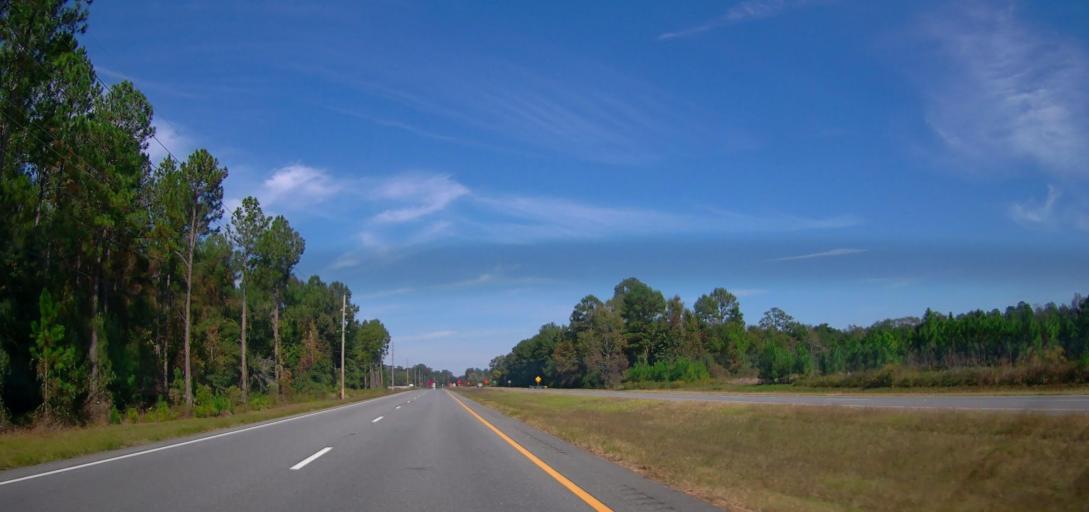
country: US
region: Georgia
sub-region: Crisp County
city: Cordele
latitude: 31.8799
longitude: -83.8968
